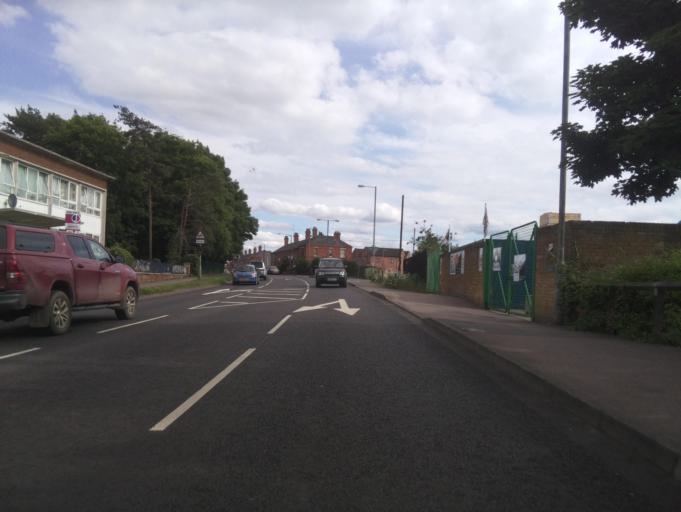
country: GB
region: England
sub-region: Worcestershire
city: Evesham
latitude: 52.1007
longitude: -1.9500
